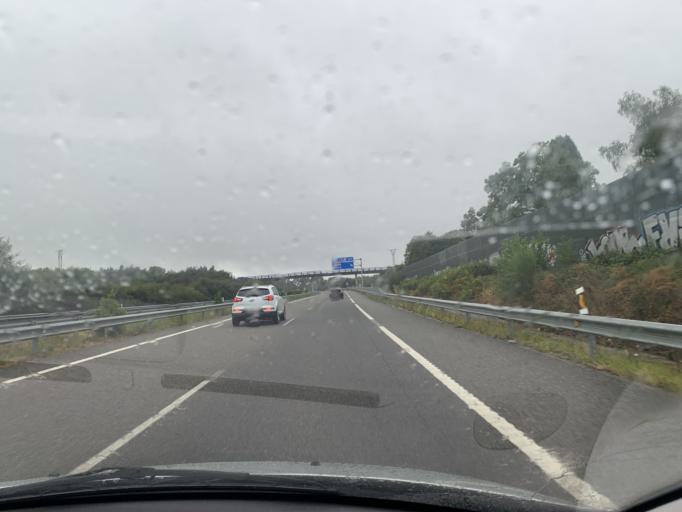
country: ES
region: Galicia
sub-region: Provincia de Lugo
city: Vilalba
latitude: 43.3275
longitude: -7.6088
